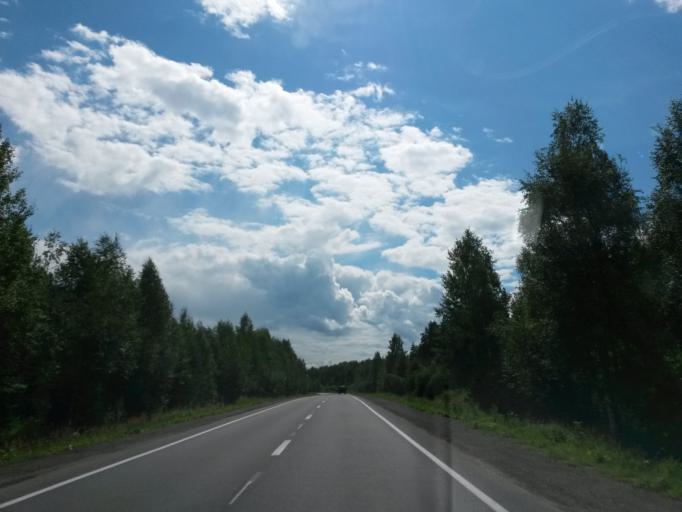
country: RU
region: Jaroslavl
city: Gavrilov-Yam
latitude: 57.2952
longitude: 39.9494
